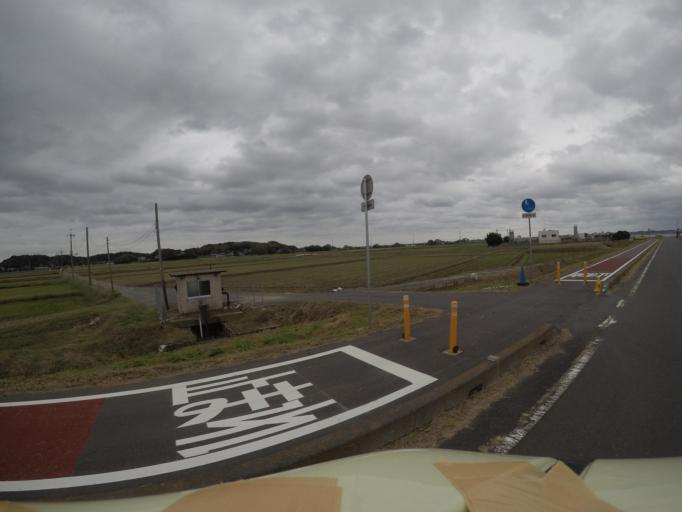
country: JP
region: Ibaraki
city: Inashiki
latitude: 36.0773
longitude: 140.3839
